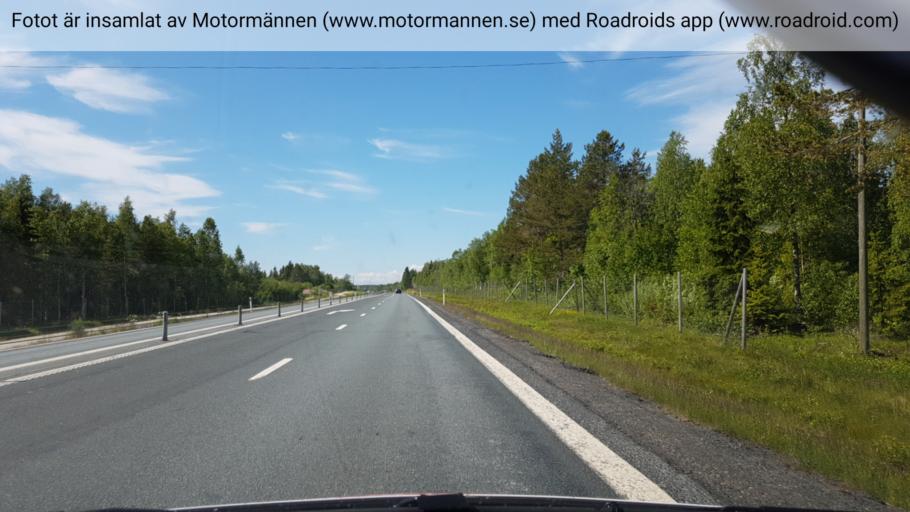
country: SE
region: Norrbotten
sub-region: Haparanda Kommun
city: Haparanda
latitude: 65.8104
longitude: 23.9545
